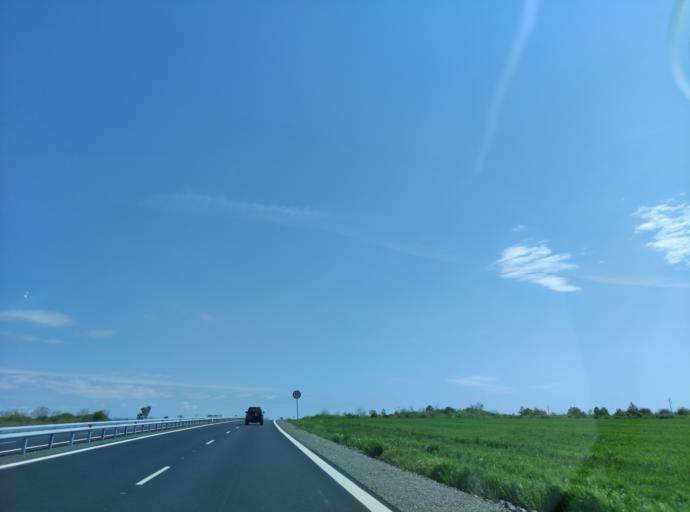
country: BG
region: Burgas
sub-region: Obshtina Pomorie
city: Pomorie
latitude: 42.5822
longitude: 27.5837
